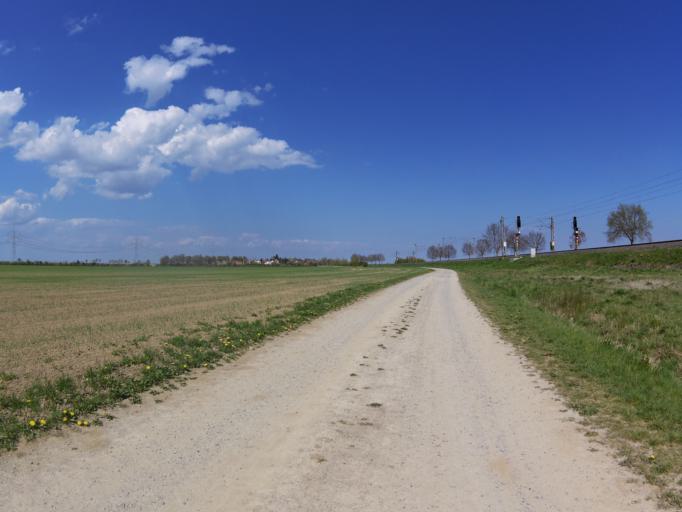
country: DE
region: Bavaria
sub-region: Regierungsbezirk Unterfranken
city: Oberpleichfeld
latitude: 49.8446
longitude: 10.1020
